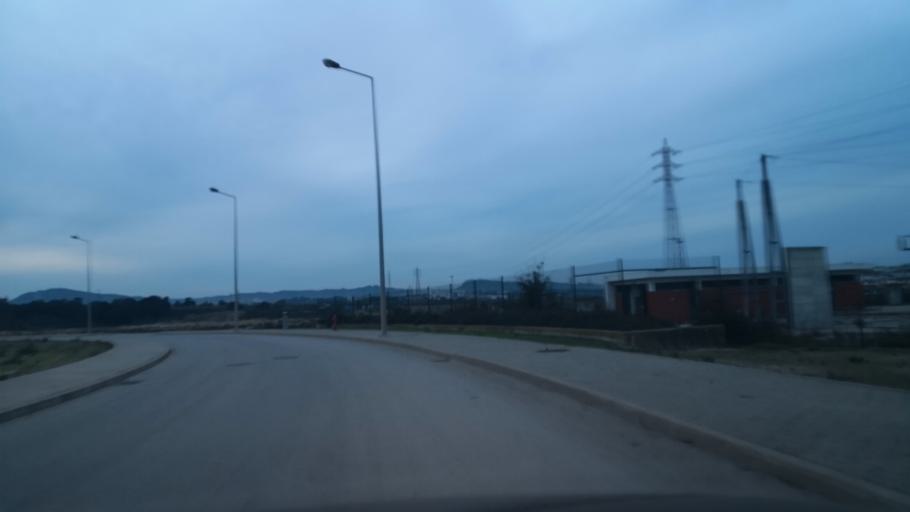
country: PT
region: Setubal
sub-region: Setubal
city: Setubal
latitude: 38.5082
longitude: -8.8325
